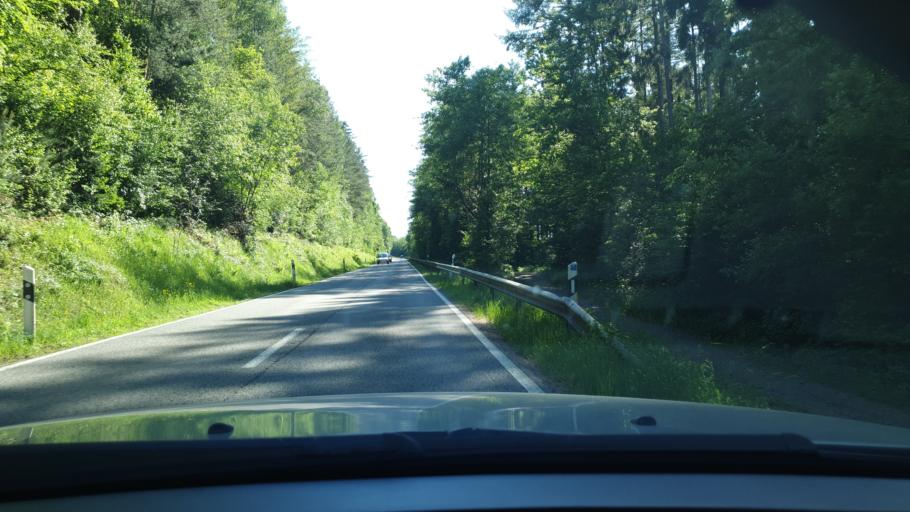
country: DE
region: Rheinland-Pfalz
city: Kaiserslautern
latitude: 49.4680
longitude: 7.7867
